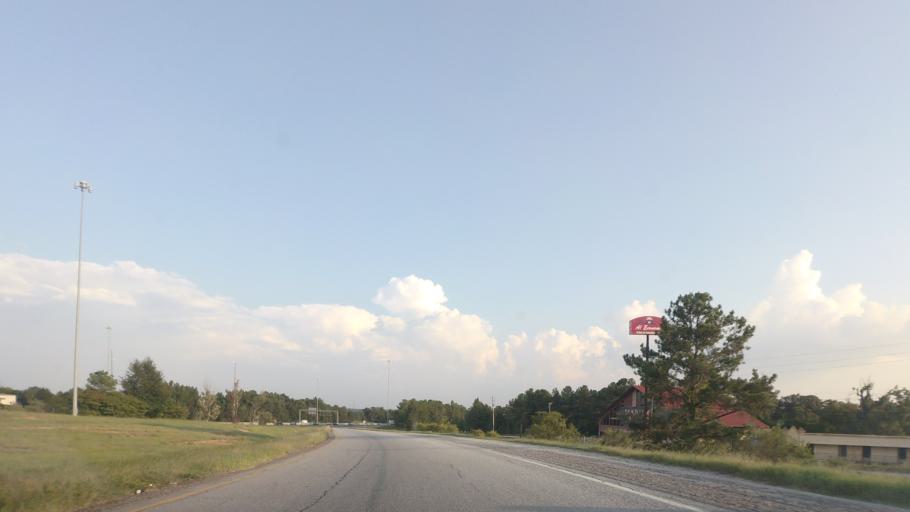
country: US
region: Georgia
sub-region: Bibb County
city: West Point
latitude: 32.8327
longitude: -83.7342
